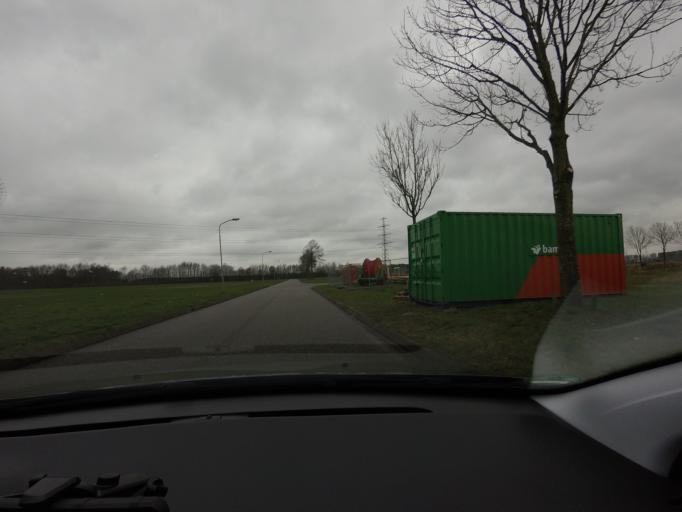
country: NL
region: Drenthe
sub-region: Gemeente Hoogeveen
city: Hoogeveen
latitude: 52.7858
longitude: 6.5004
